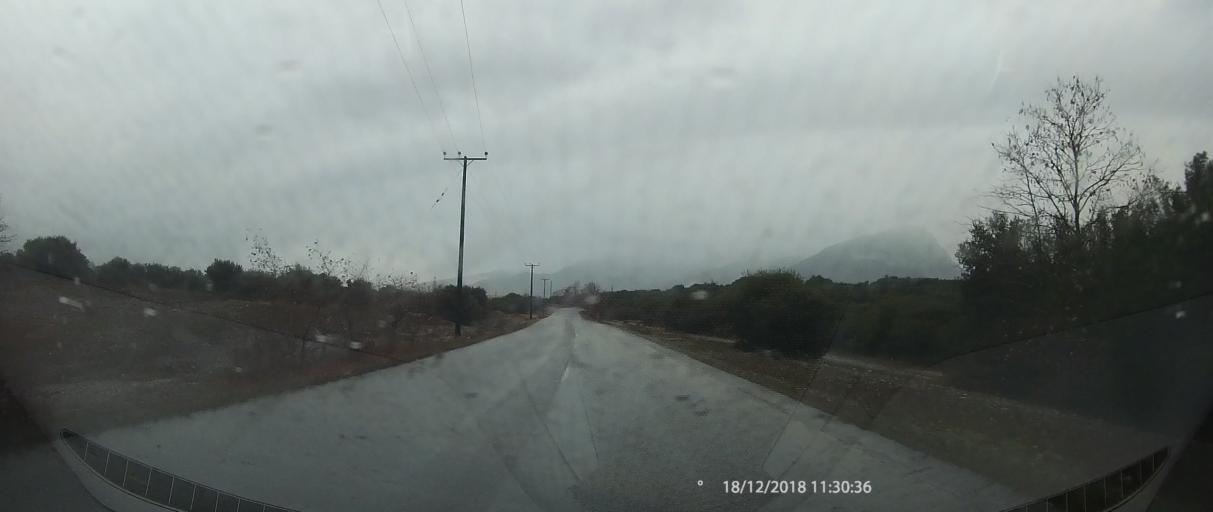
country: GR
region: Central Macedonia
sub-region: Nomos Pierias
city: Litochoro
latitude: 40.1209
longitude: 22.5200
